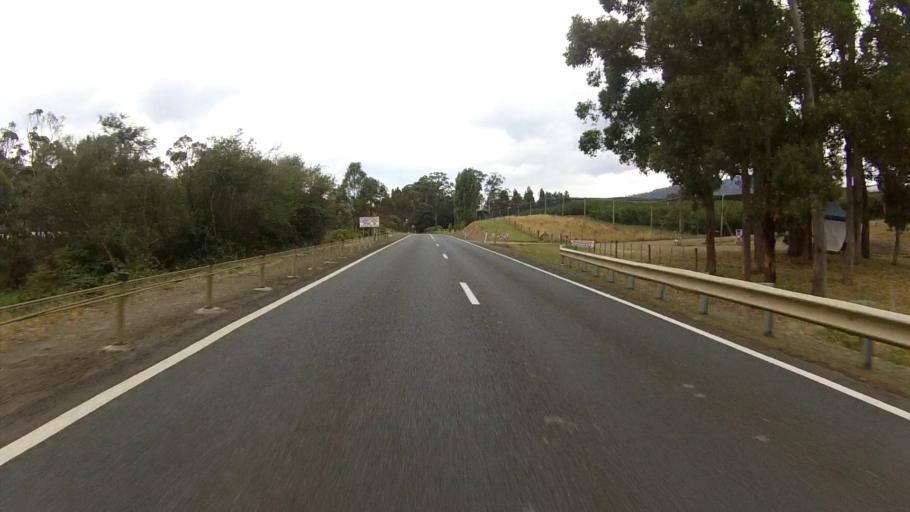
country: AU
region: Tasmania
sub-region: Huon Valley
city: Franklin
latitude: -43.0799
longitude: 147.0320
